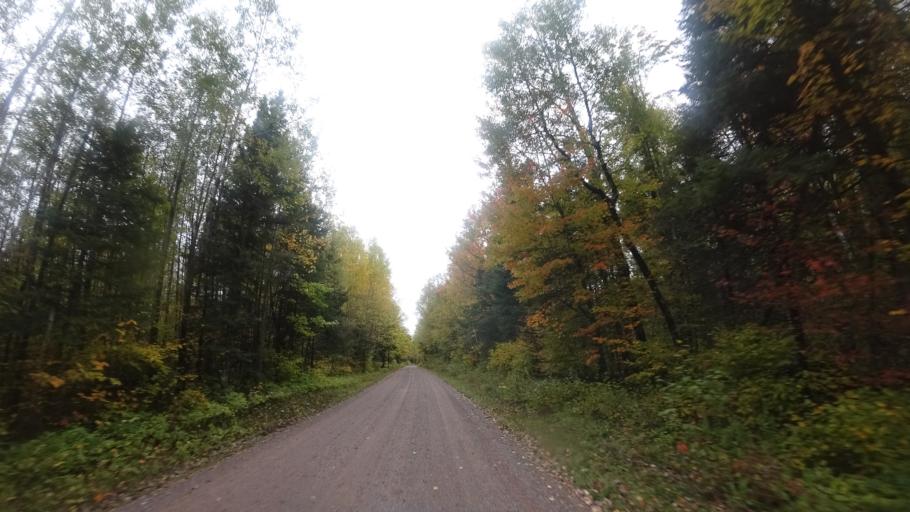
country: US
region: Wisconsin
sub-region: Sawyer County
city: Little Round Lake
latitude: 46.0502
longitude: -90.9892
